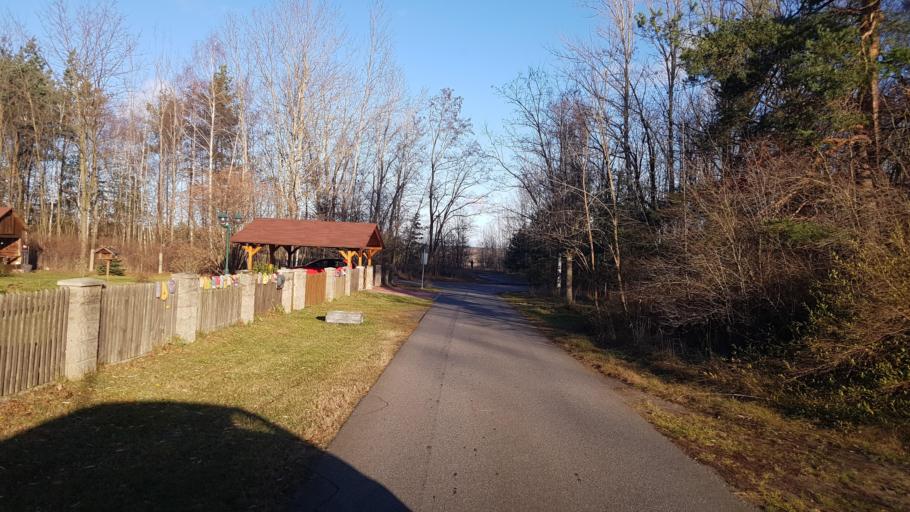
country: DE
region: Brandenburg
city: Heinersbruck
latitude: 51.7448
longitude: 14.5137
